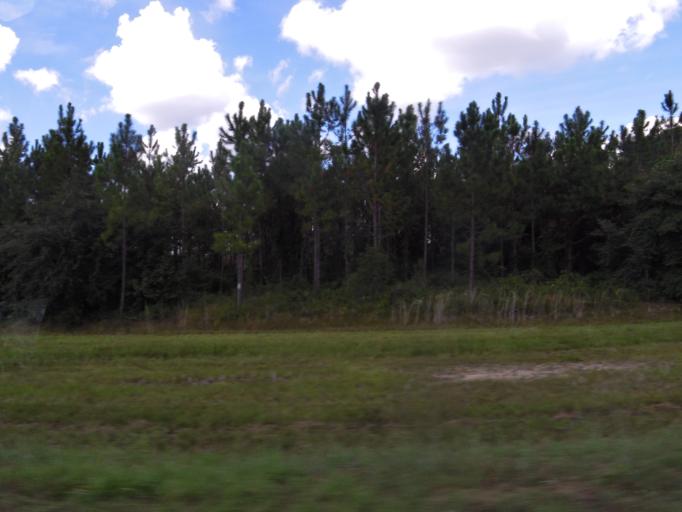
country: US
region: Florida
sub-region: Hamilton County
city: Jasper
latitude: 30.6773
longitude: -82.7041
